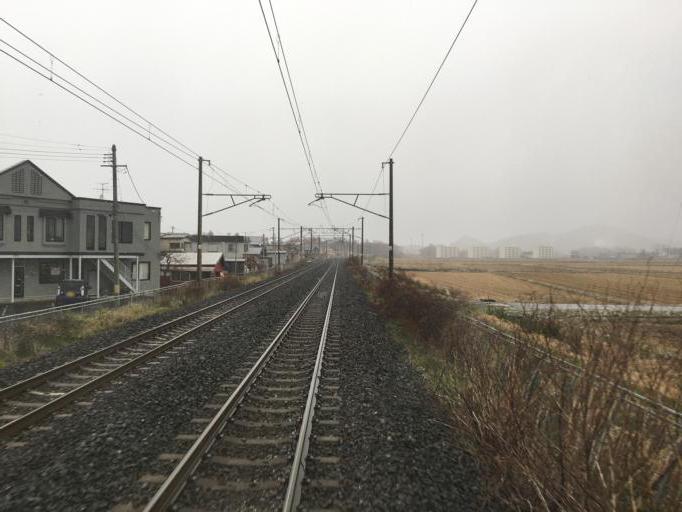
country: JP
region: Aomori
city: Aomori Shi
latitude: 40.8361
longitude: 140.8082
